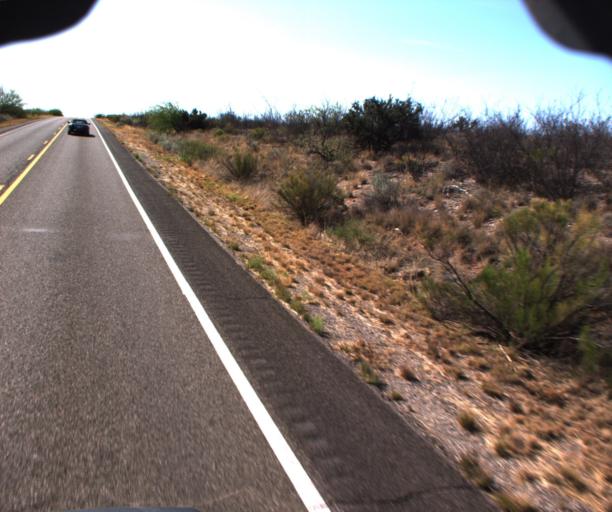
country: US
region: Arizona
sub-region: Cochise County
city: Tombstone
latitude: 31.7708
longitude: -110.1248
